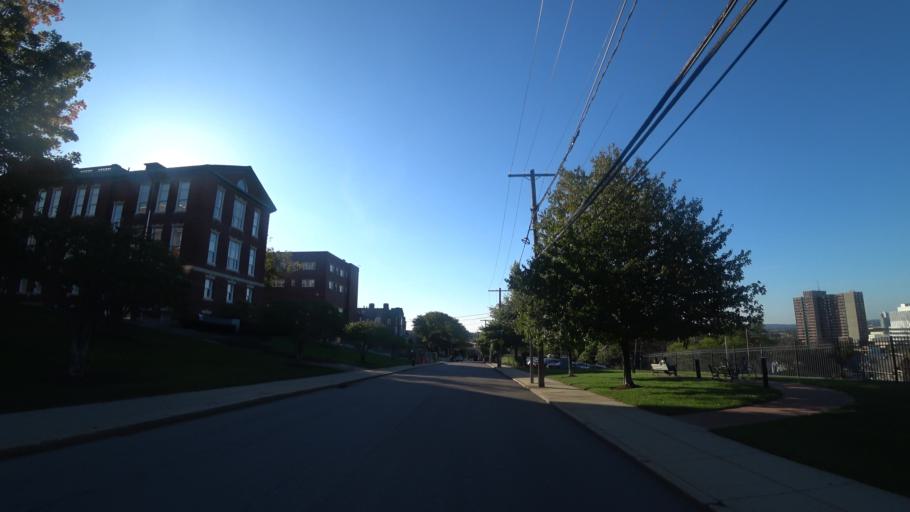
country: US
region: Massachusetts
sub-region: Norfolk County
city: Brookline
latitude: 42.3301
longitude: -71.1065
